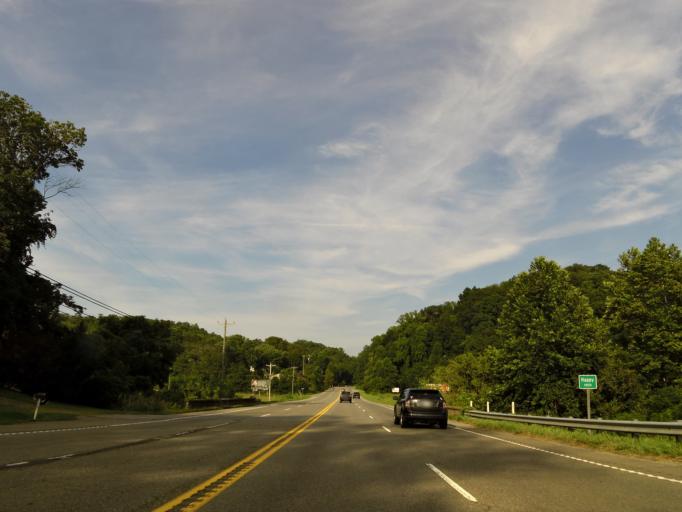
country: US
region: Tennessee
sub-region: Sevier County
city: Seymour
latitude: 35.8477
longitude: -83.7082
